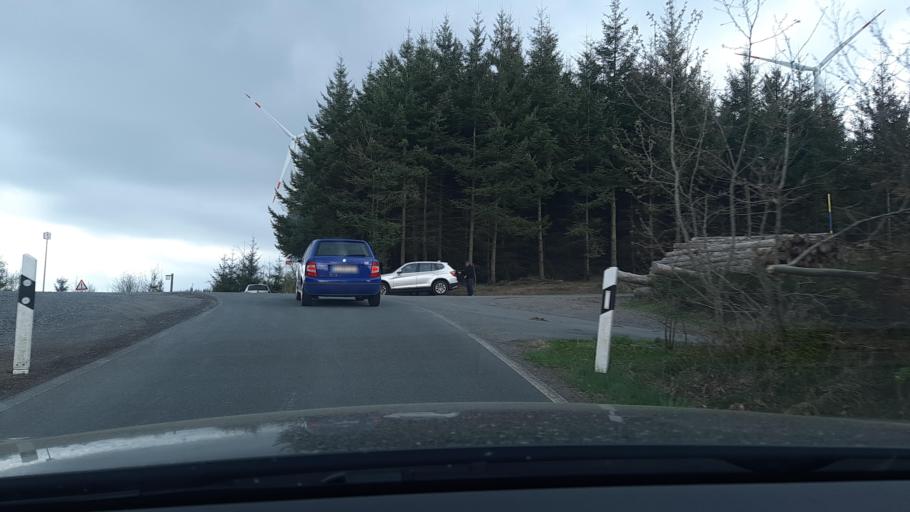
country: DE
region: North Rhine-Westphalia
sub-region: Regierungsbezirk Arnsberg
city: Bad Laasphe
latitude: 50.8930
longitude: 8.3865
